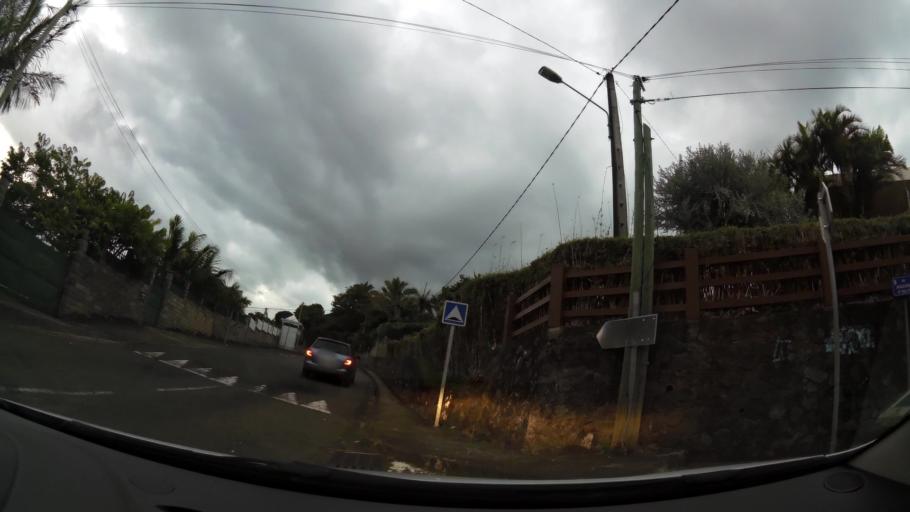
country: RE
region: Reunion
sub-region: Reunion
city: Saint-Denis
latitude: -20.9074
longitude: 55.4676
